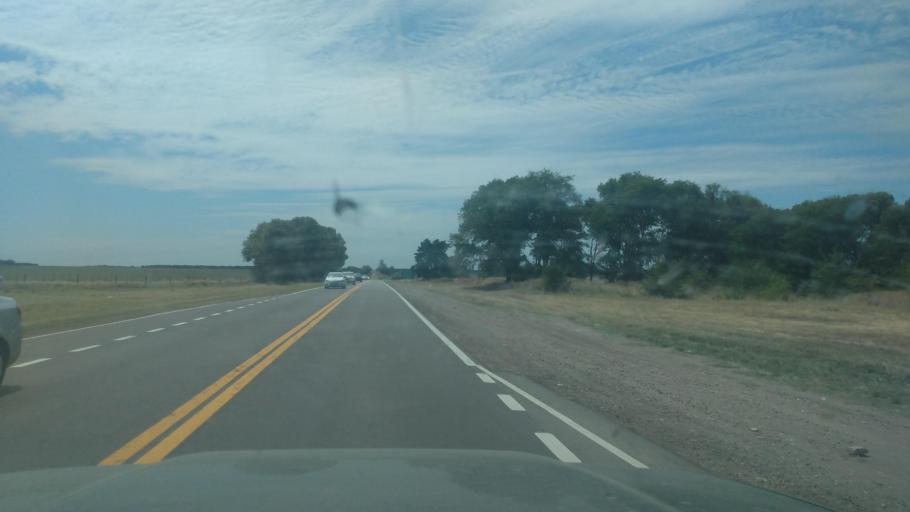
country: AR
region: La Pampa
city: Doblas
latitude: -37.1192
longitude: -64.2859
